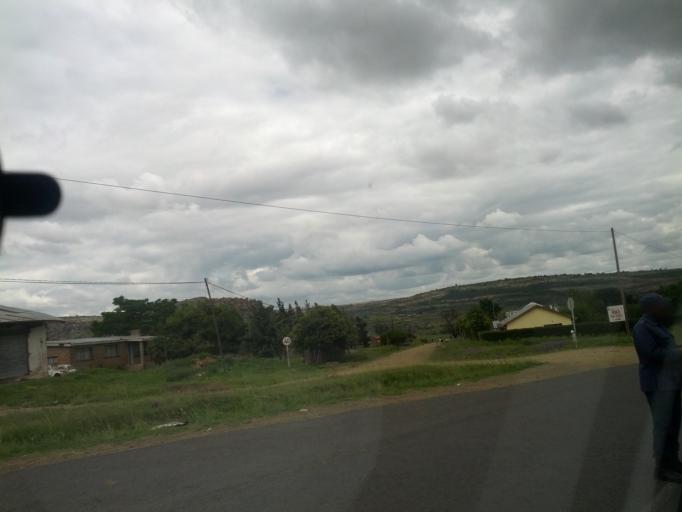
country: LS
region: Berea
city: Teyateyaneng
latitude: -29.1471
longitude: 27.7212
